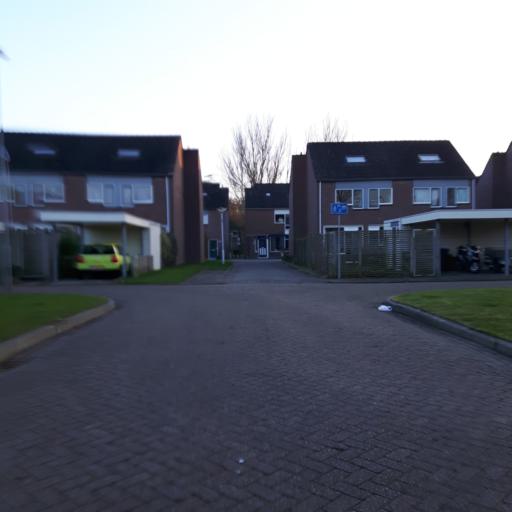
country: NL
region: Zeeland
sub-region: Gemeente Goes
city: Goes
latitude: 51.5161
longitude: 3.8762
